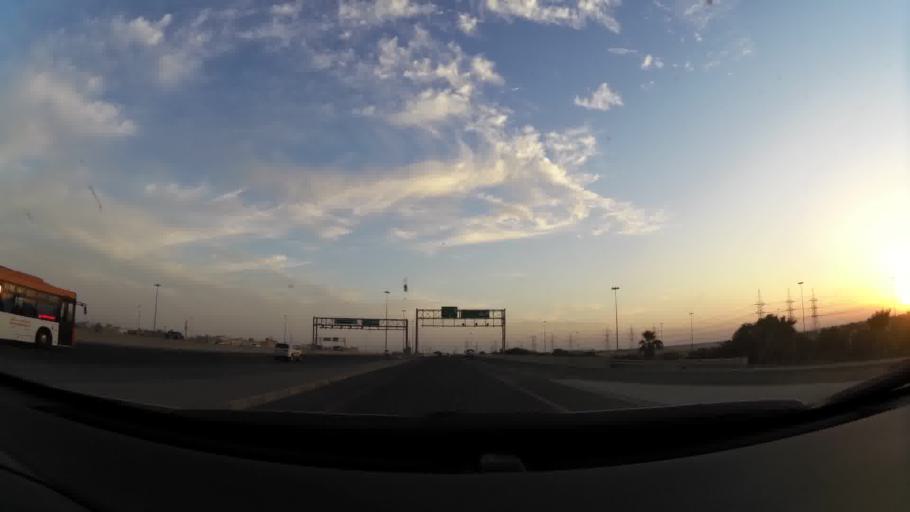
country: KW
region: Muhafazat al Jahra'
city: Al Jahra'
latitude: 29.3129
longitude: 47.7847
